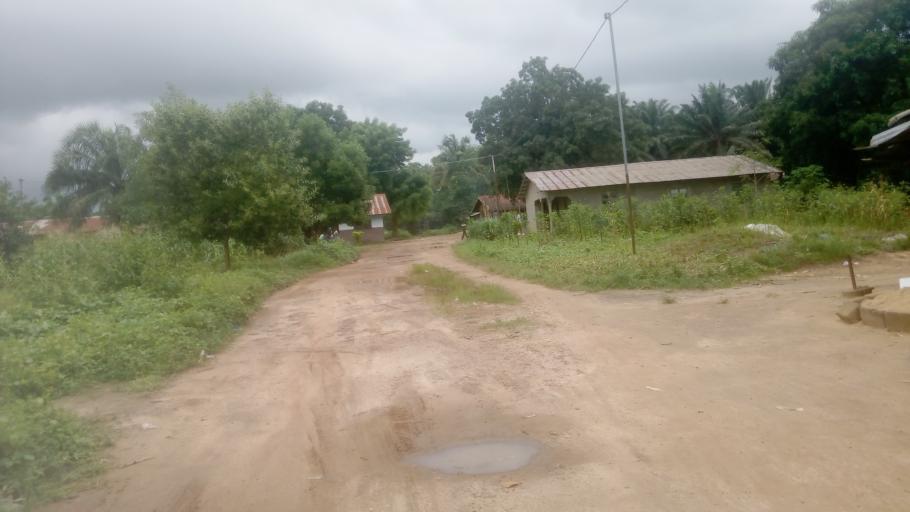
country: SL
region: Northern Province
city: Lunsar
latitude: 8.6849
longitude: -12.5469
